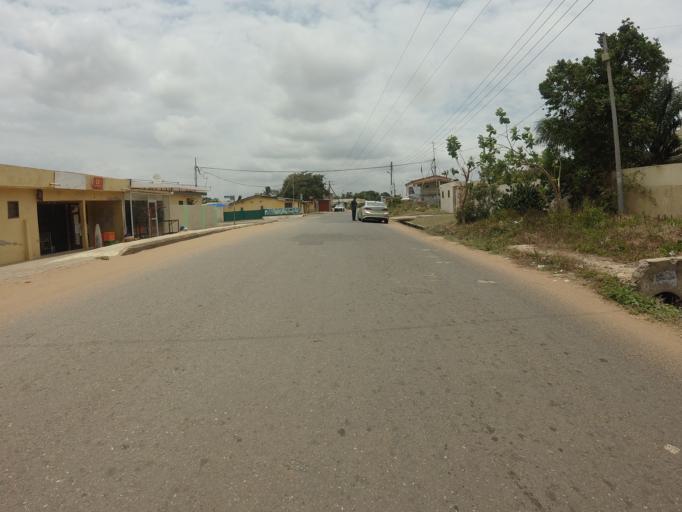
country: GH
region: Greater Accra
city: Nungua
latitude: 5.6145
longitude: -0.0785
